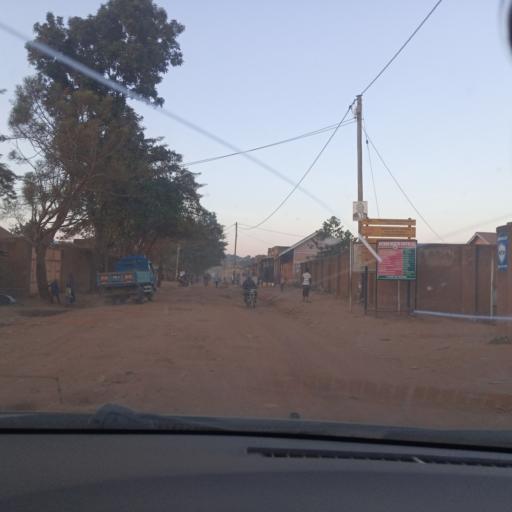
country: UG
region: Central Region
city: Masaka
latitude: -0.3231
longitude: 31.7620
